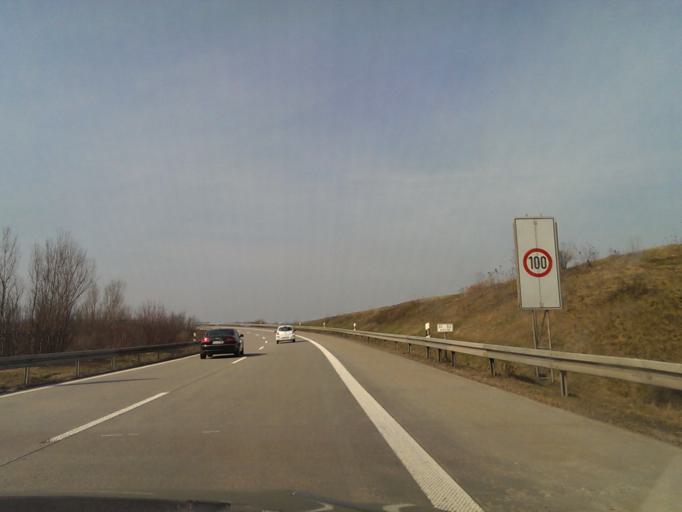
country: DE
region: Saxony
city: Wittgensdorf
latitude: 50.8529
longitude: 12.8514
